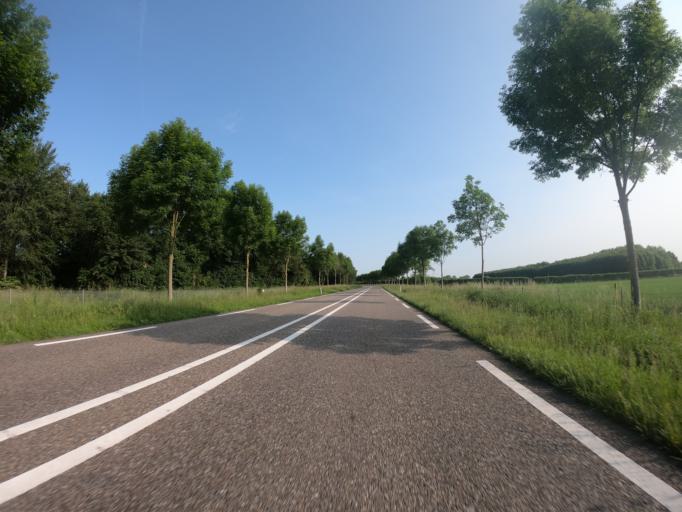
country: NL
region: North Brabant
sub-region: Gemeente Landerd
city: Reek
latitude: 51.7821
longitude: 5.6652
